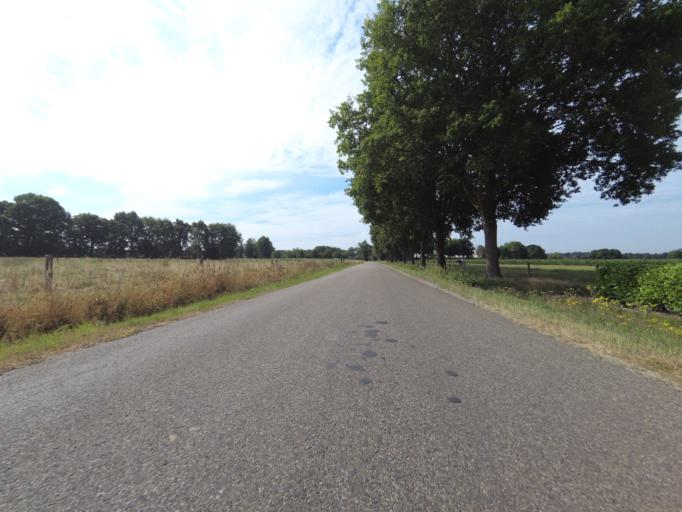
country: NL
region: Gelderland
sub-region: Gemeente Ede
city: Wekerom
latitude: 52.1000
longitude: 5.7314
